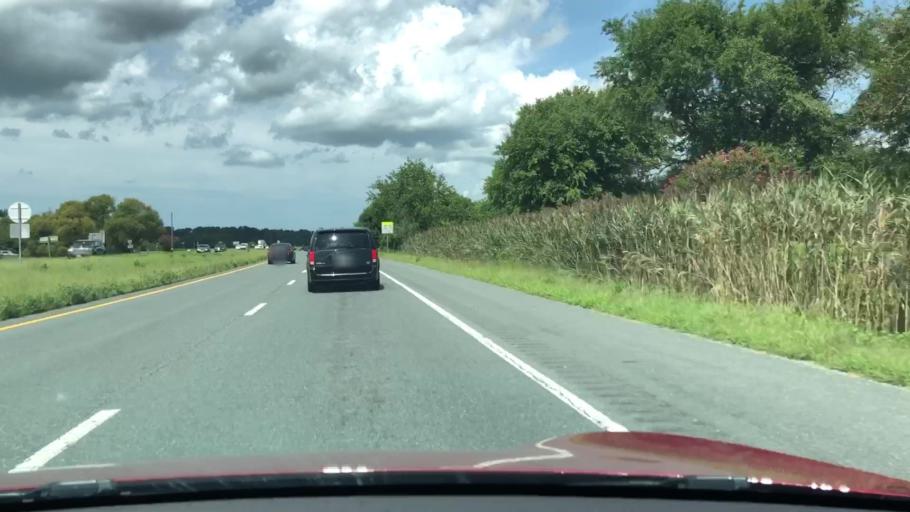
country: US
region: Virginia
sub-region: Northampton County
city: Cape Charles
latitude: 37.2735
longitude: -75.9756
